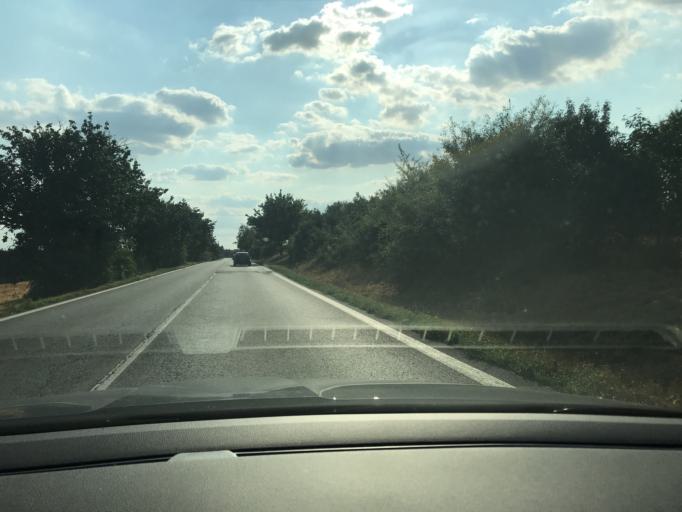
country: CZ
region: Central Bohemia
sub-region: Okres Kladno
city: Slany
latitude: 50.2412
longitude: 14.1350
